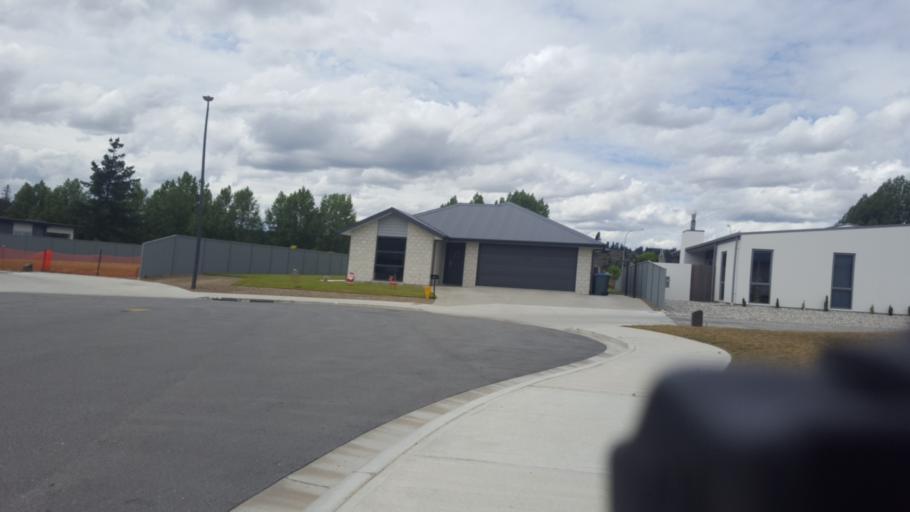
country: NZ
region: Otago
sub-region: Queenstown-Lakes District
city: Wanaka
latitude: -45.2423
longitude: 169.3755
